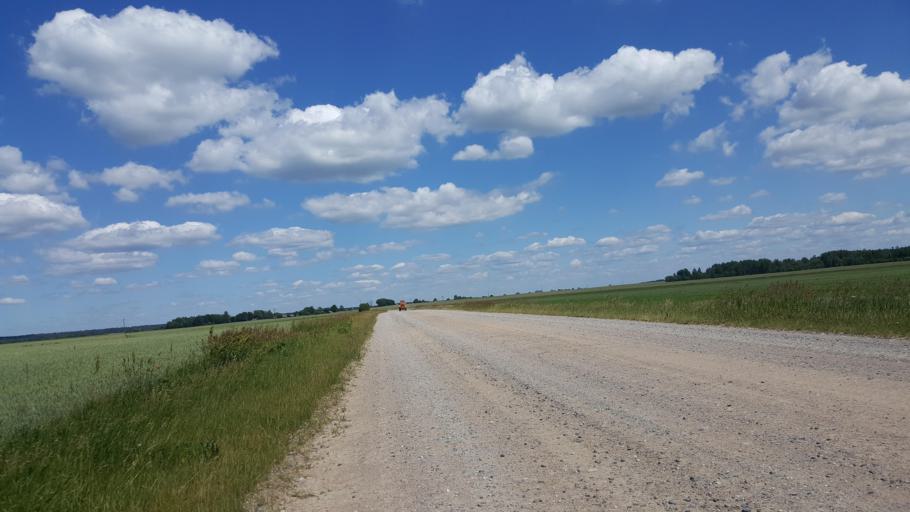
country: PL
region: Podlasie
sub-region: Powiat hajnowski
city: Czeremcha
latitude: 52.4917
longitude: 23.4537
